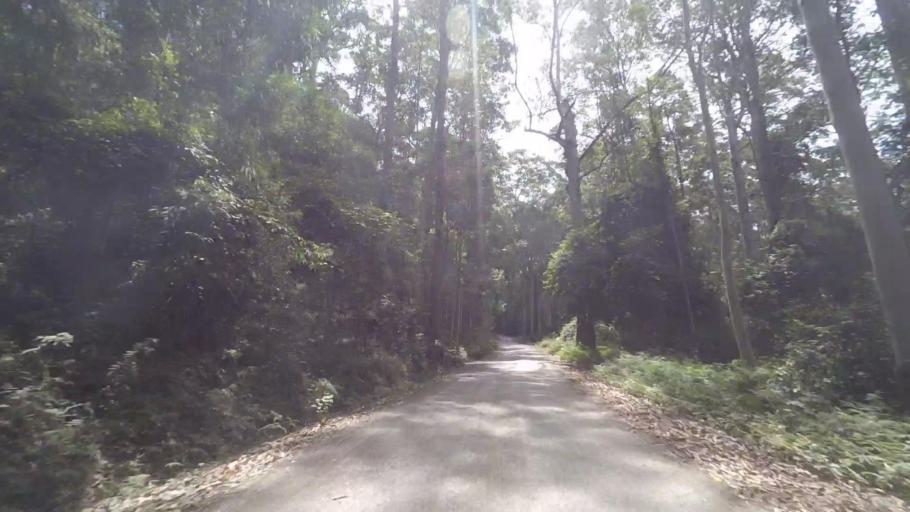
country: AU
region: New South Wales
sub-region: Shoalhaven Shire
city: Milton
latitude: -35.4414
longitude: 150.3155
